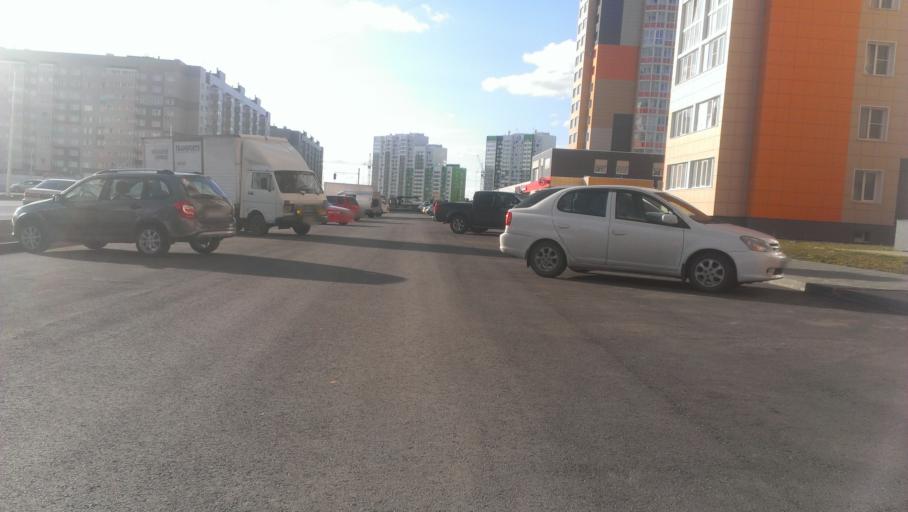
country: RU
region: Altai Krai
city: Novosilikatnyy
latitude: 53.3376
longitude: 83.6560
